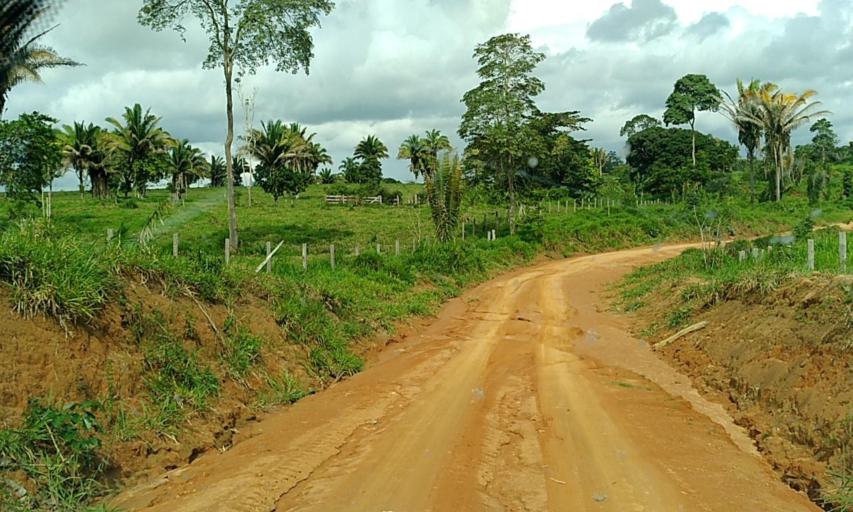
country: BR
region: Para
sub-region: Altamira
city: Altamira
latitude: -3.2314
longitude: -52.7294
